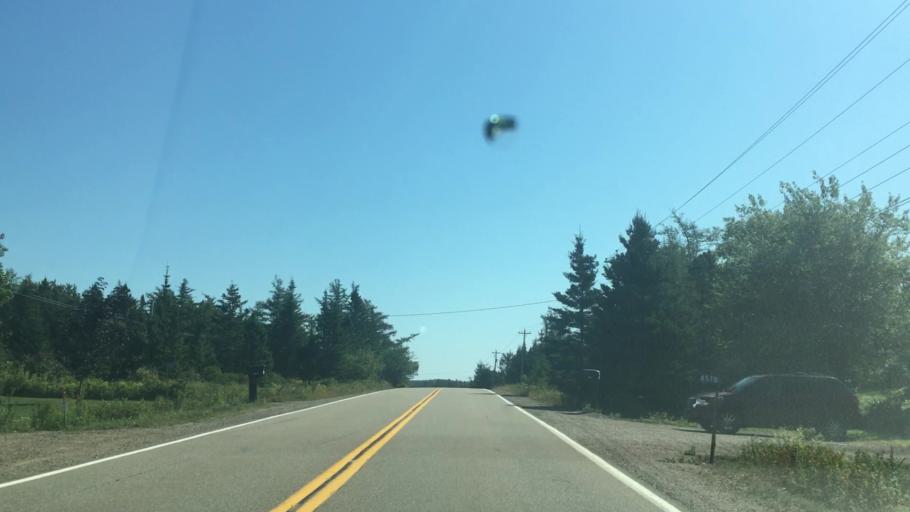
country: CA
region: Nova Scotia
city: Antigonish
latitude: 45.0242
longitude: -62.0233
